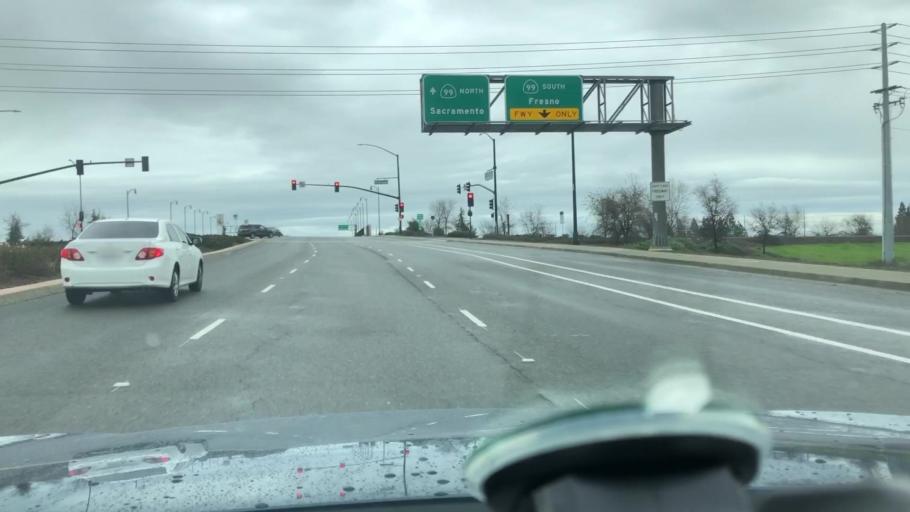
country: US
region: California
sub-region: Sacramento County
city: Elk Grove
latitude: 38.3750
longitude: -121.3641
